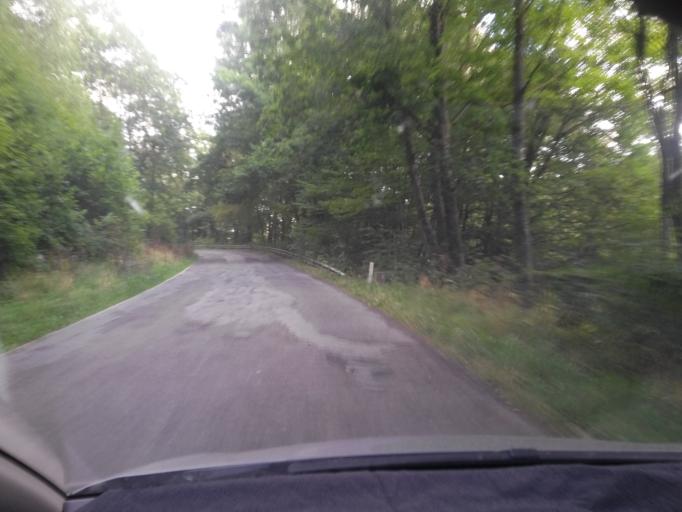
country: BE
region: Wallonia
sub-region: Province du Luxembourg
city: Libin
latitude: 50.0228
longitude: 5.2998
